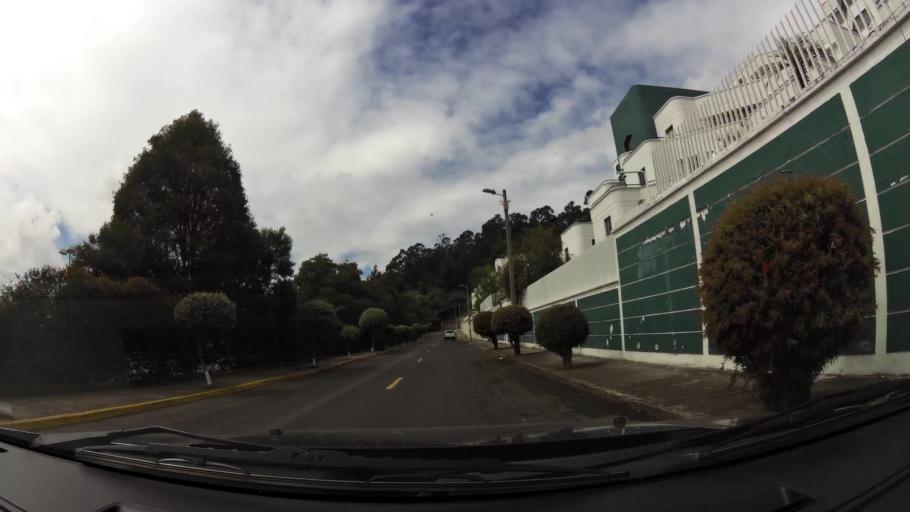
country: EC
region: Pichincha
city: Quito
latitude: -0.1621
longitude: -78.4994
